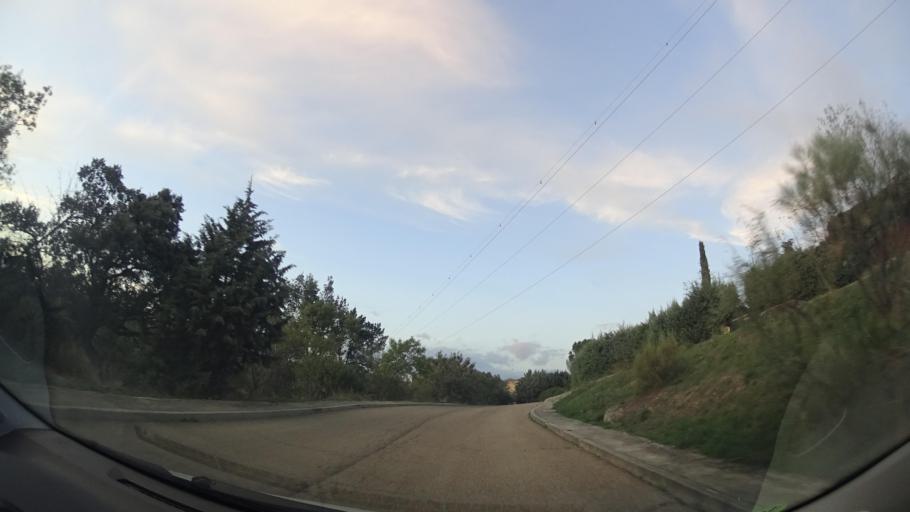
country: ES
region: Madrid
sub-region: Provincia de Madrid
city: Colmenarejo
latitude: 40.5603
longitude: -4.0231
